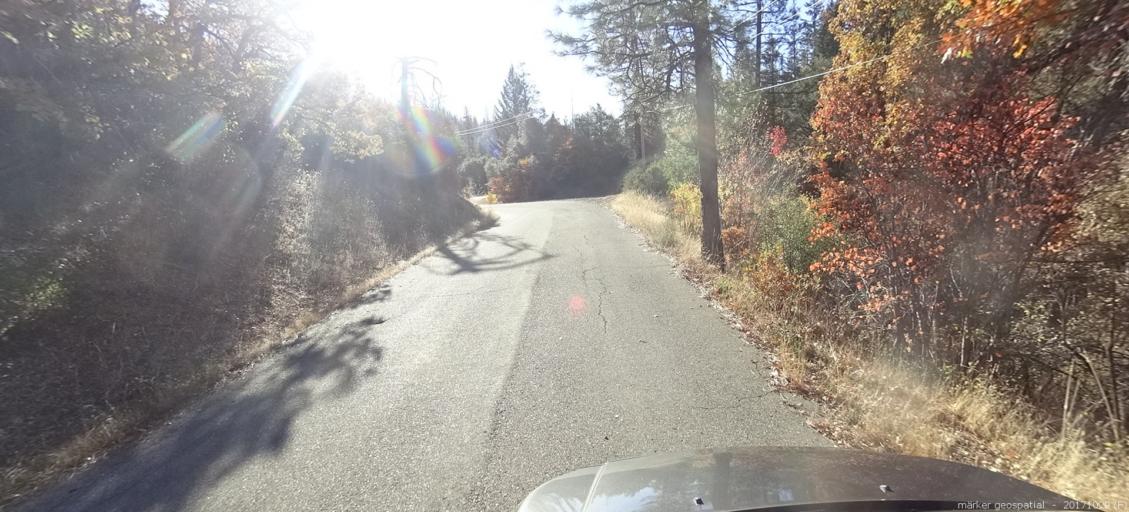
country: US
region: California
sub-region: Trinity County
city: Hayfork
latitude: 40.3803
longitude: -122.9797
